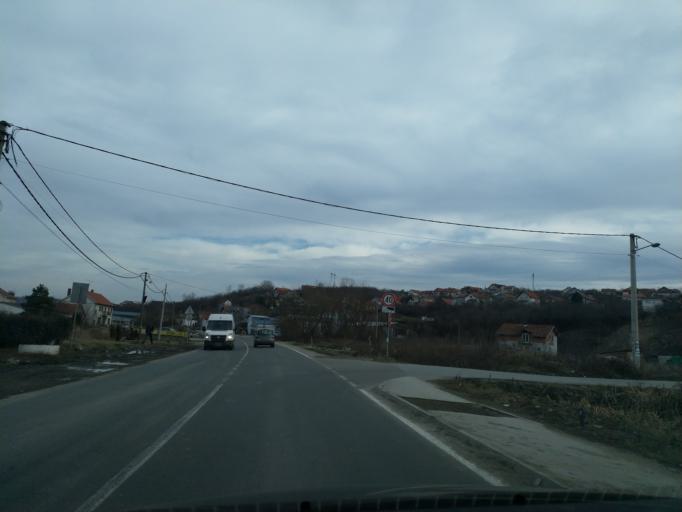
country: RS
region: Central Serbia
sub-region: Belgrade
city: Zvezdara
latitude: 44.7277
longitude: 20.5768
